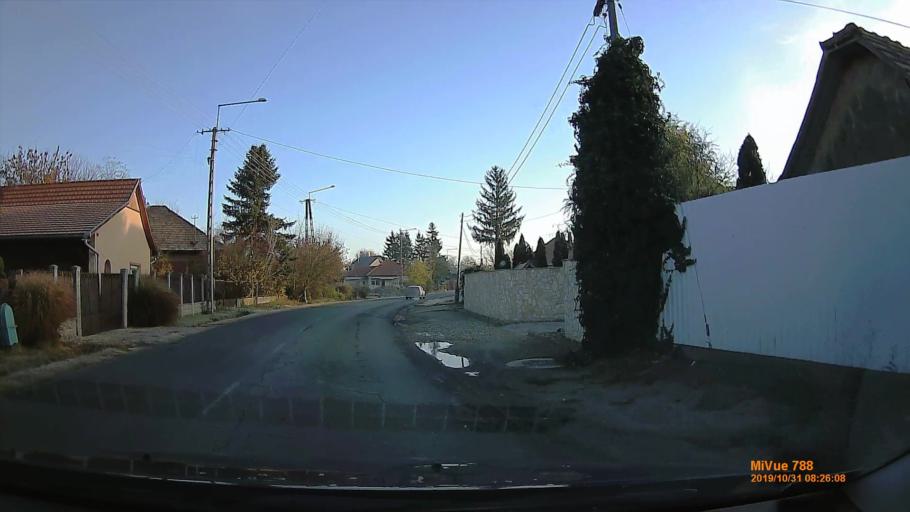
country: HU
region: Pest
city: Tapiobicske
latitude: 47.3644
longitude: 19.6754
